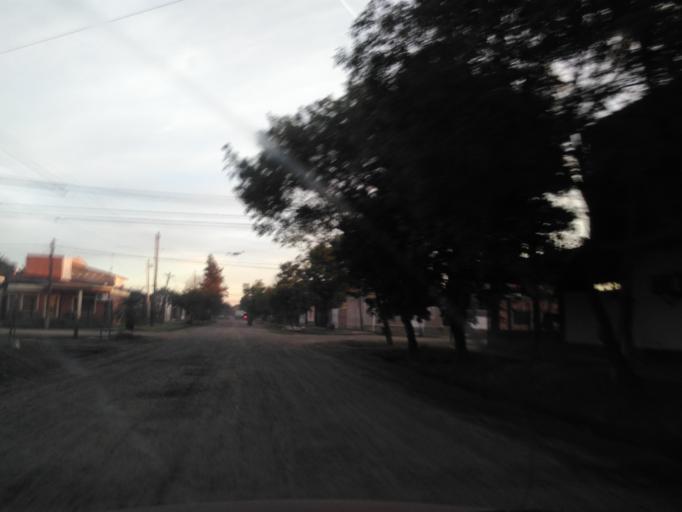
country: AR
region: Chaco
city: Resistencia
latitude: -27.4705
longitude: -58.9953
